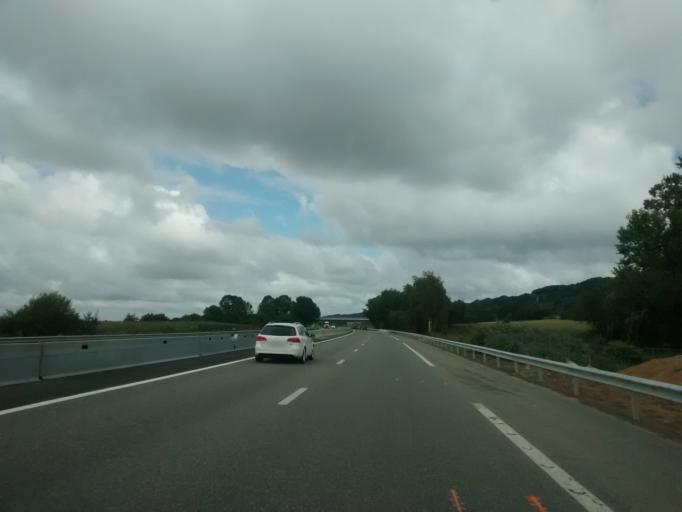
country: FR
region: Aquitaine
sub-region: Departement des Pyrenees-Atlantiques
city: Denguin
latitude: 43.3686
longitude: -0.4821
